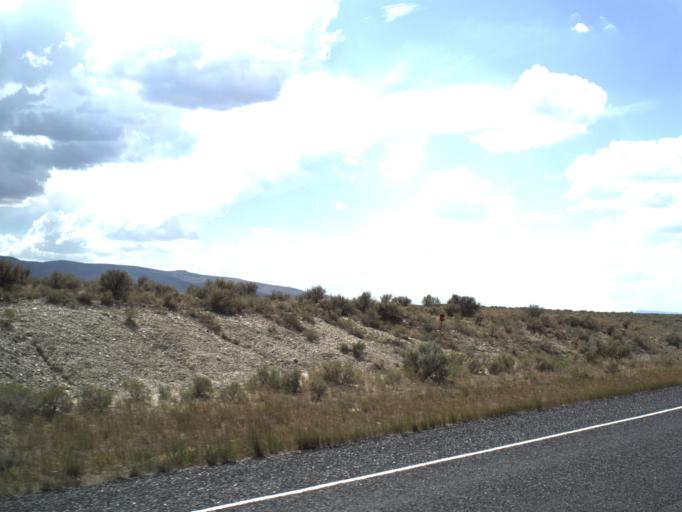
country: US
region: Idaho
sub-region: Minidoka County
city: Rupert
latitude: 41.9840
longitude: -113.1731
